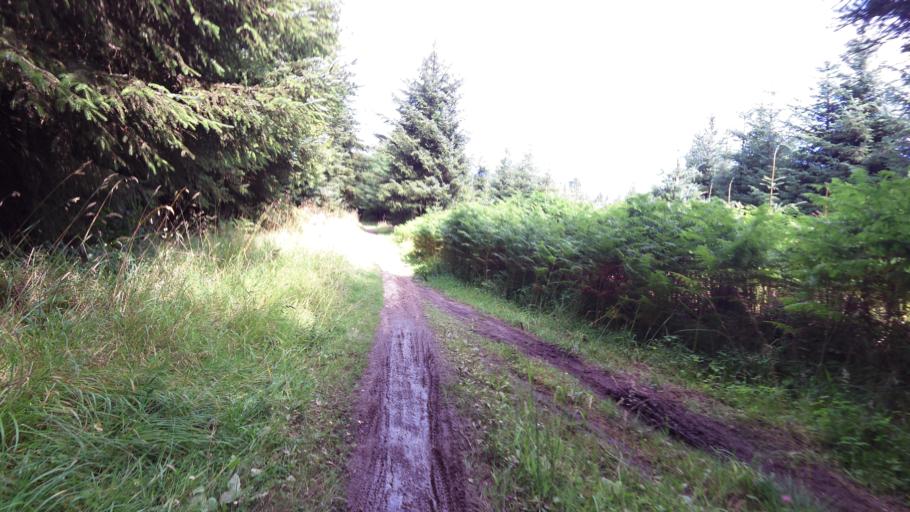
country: GB
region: England
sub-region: North Yorkshire
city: Thornton Dale
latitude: 54.3073
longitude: -0.6380
